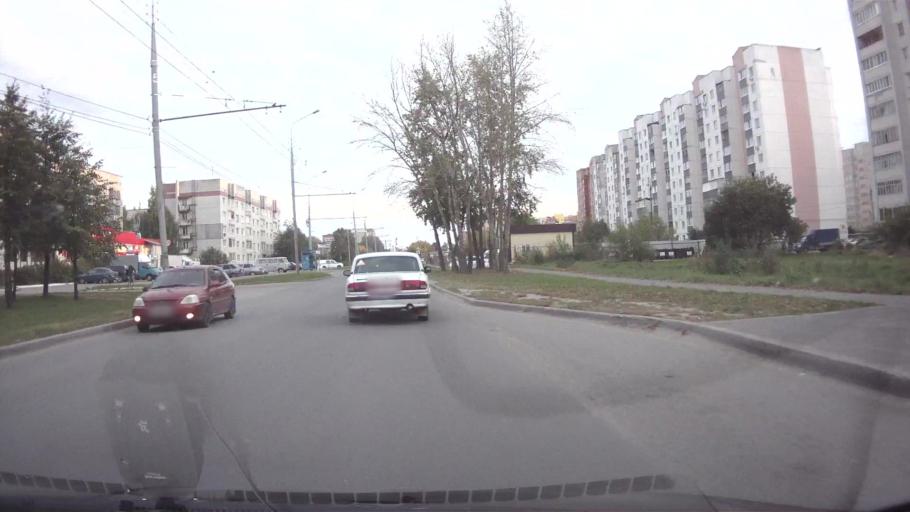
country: RU
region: Mariy-El
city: Yoshkar-Ola
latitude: 56.6513
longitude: 47.8549
